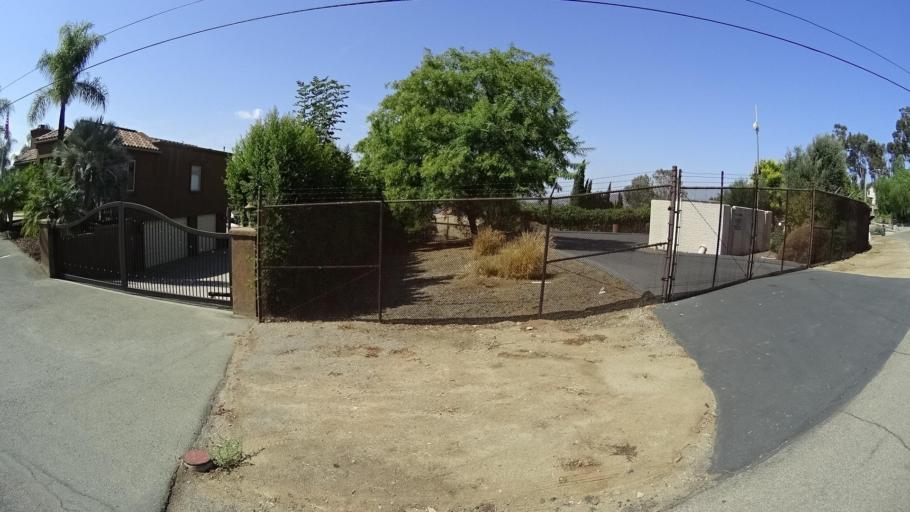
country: US
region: California
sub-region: San Diego County
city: Granite Hills
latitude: 32.7802
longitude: -116.9180
